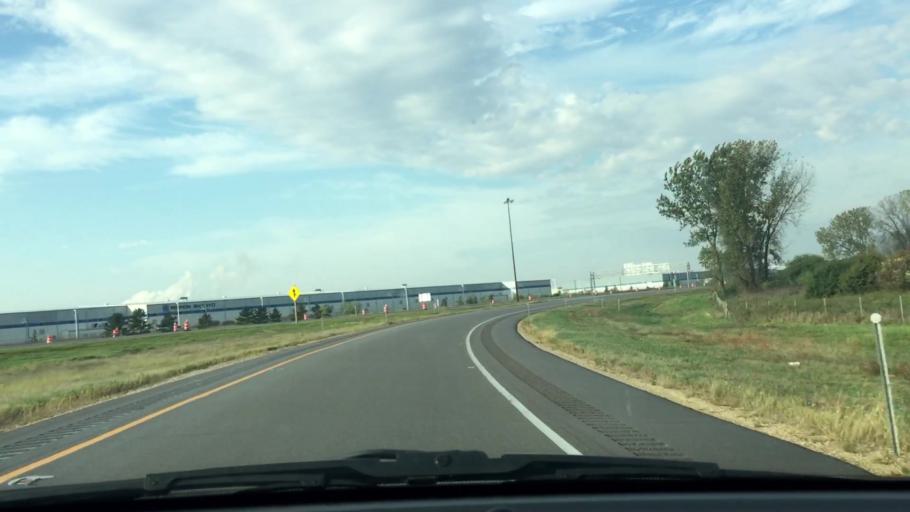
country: US
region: Illinois
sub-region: Ogle County
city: Rochelle
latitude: 41.9053
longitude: -89.0259
